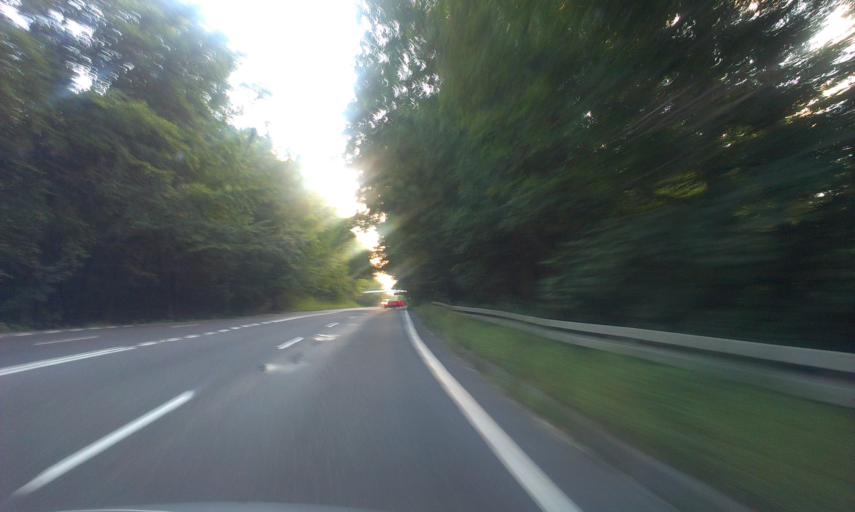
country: PL
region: West Pomeranian Voivodeship
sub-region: Koszalin
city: Koszalin
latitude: 54.2102
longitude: 16.2169
